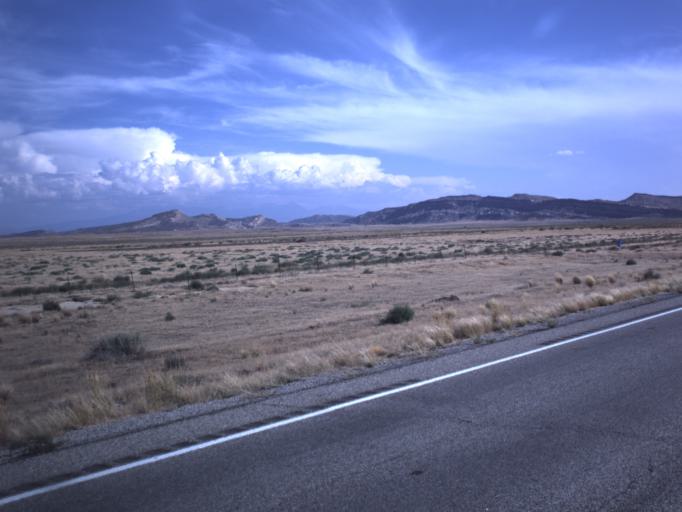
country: US
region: Utah
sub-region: Grand County
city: Moab
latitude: 38.9151
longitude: -109.8150
